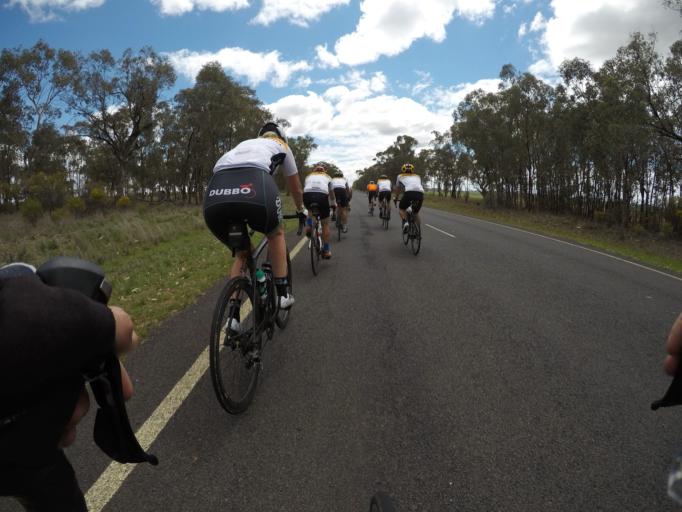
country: AU
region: New South Wales
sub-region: Dubbo Municipality
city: Dubbo
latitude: -32.4127
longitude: 148.5708
